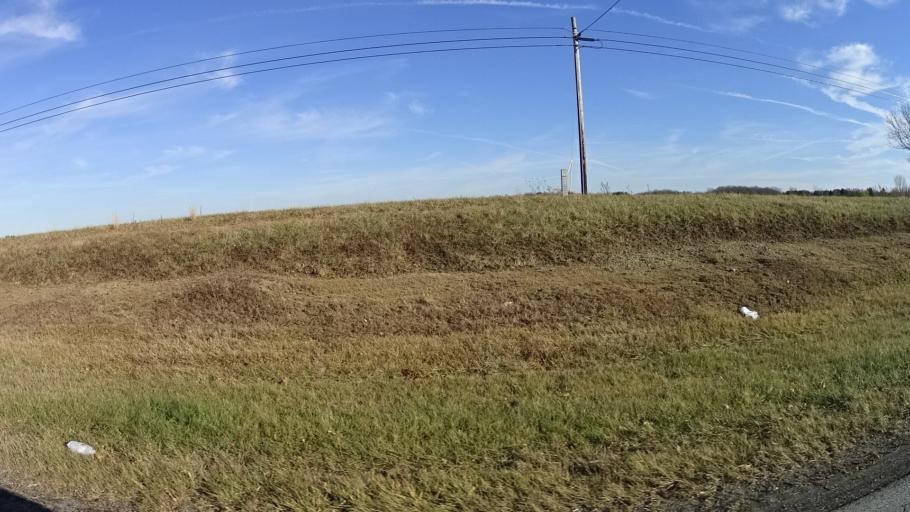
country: US
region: Ohio
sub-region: Lorain County
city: Wellington
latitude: 41.1946
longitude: -82.2168
